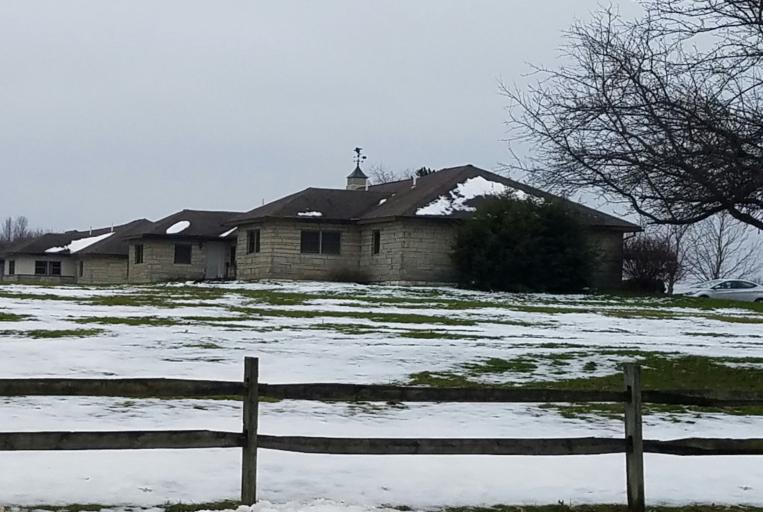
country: US
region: Pennsylvania
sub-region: Mercer County
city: Mercer
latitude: 41.3179
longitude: -80.2602
